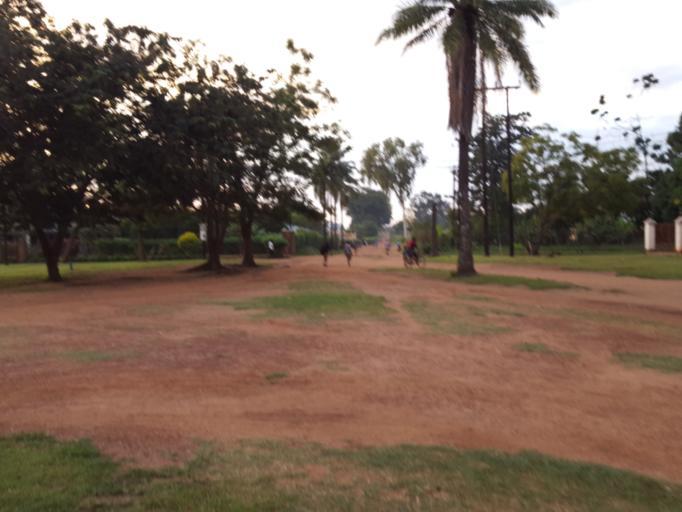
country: UG
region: Northern Region
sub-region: Yumbe District
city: Yumbe
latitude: 3.4186
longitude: 31.1160
